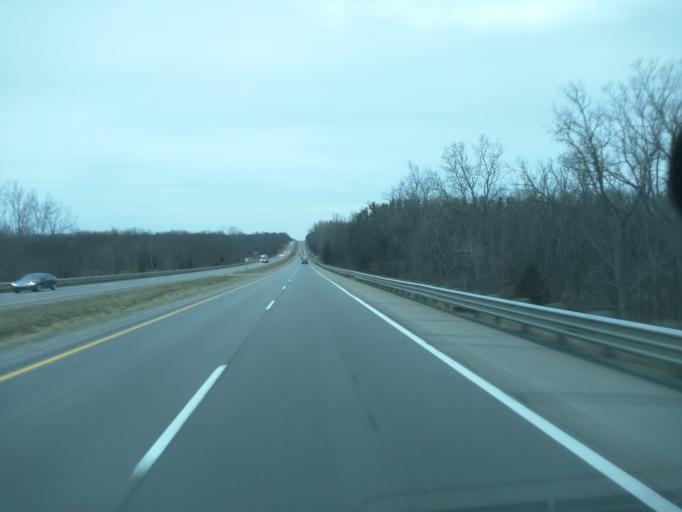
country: US
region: Michigan
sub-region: Ingham County
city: Leslie
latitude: 42.4078
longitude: -84.4293
